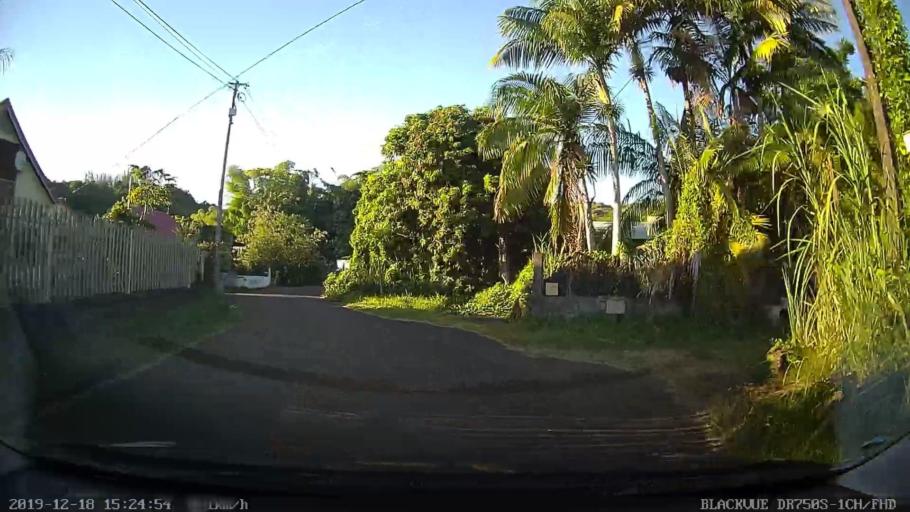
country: RE
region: Reunion
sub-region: Reunion
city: Bras-Panon
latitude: -21.0013
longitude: 55.6532
